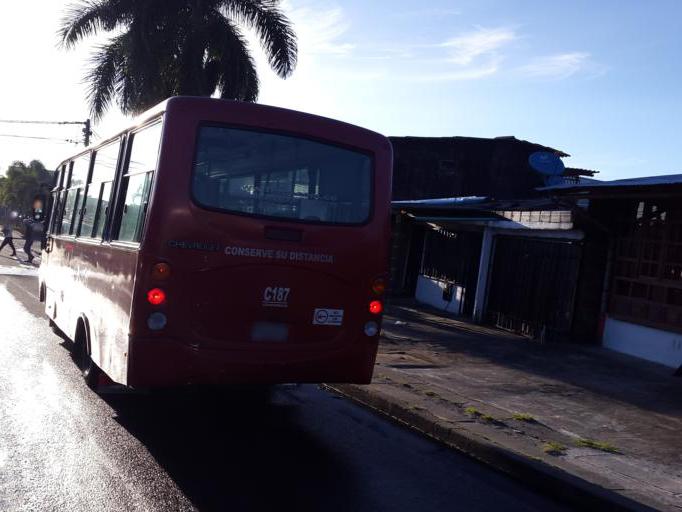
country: CO
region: Quindio
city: Armenia
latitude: 4.5316
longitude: -75.6928
